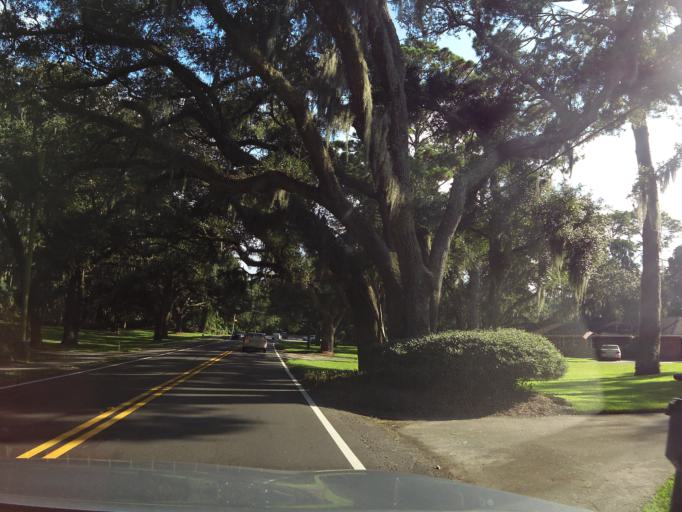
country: US
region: Georgia
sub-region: Glynn County
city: Saint Simons Island
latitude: 31.1757
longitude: -81.3779
